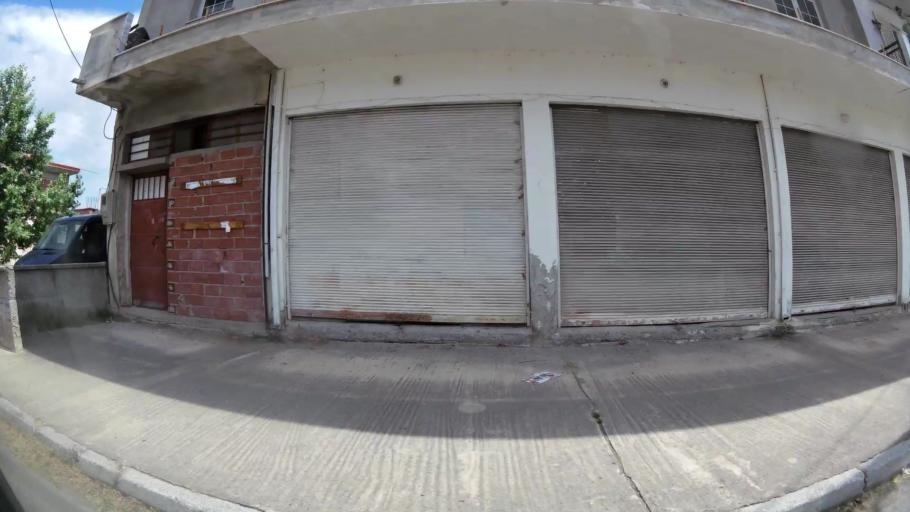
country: GR
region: Central Macedonia
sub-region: Nomos Pierias
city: Katerini
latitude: 40.2760
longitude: 22.4954
